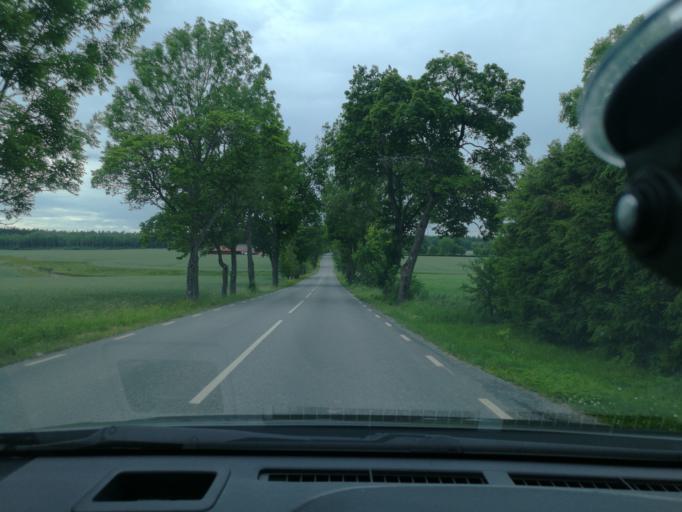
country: SE
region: Vaestmanland
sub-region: Vasteras
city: Skultuna
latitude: 59.7739
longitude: 16.3863
